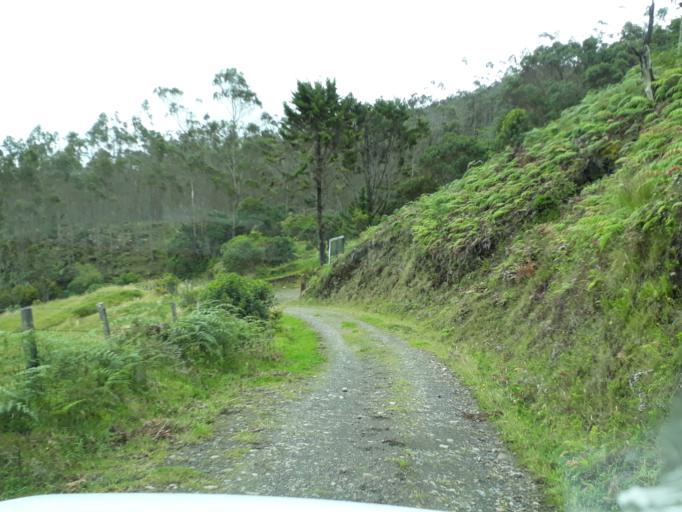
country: CO
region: Cundinamarca
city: Junin
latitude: 4.7334
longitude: -73.6258
